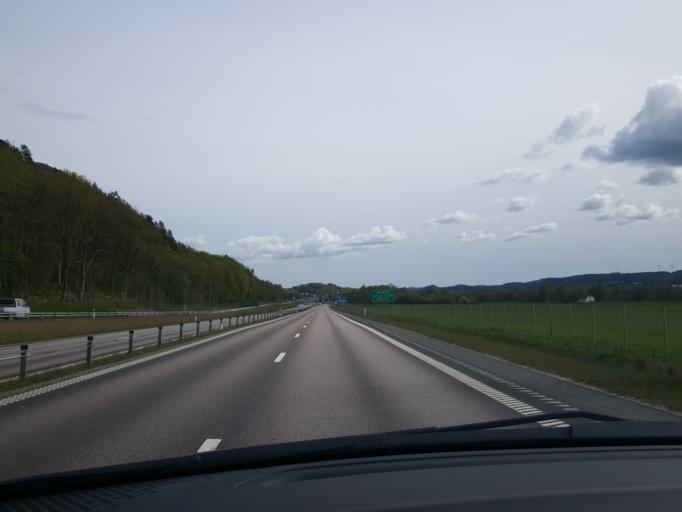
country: SE
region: Vaestra Goetaland
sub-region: Lilla Edets Kommun
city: Lilla Edet
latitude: 58.1590
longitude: 12.1360
